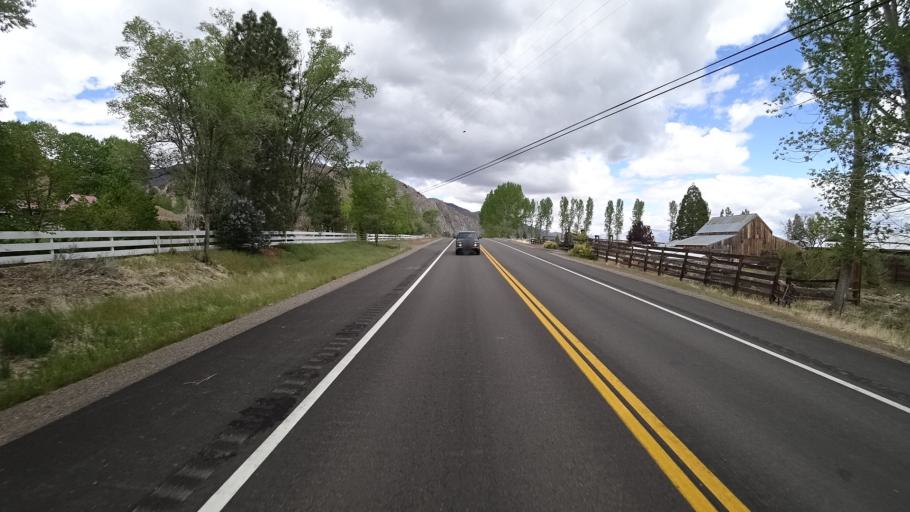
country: US
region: Nevada
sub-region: Lyon County
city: Smith Valley
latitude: 38.5384
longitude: -119.4960
